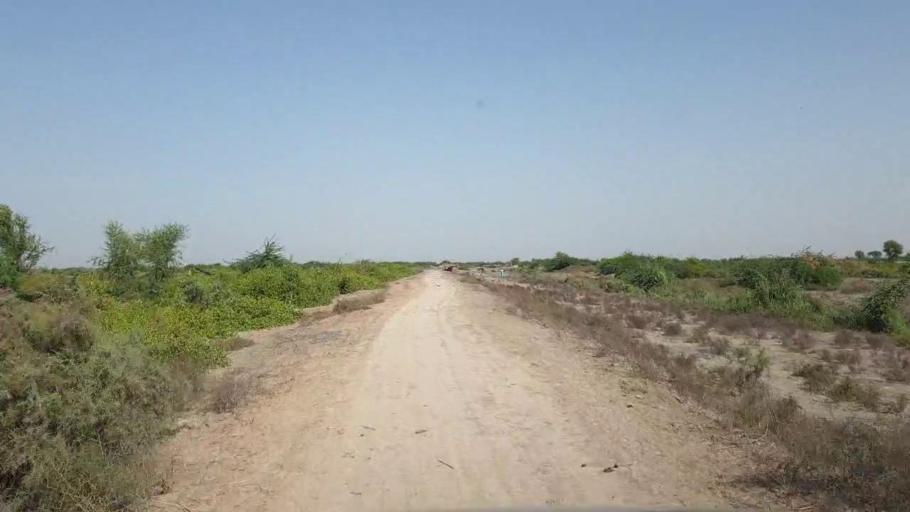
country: PK
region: Sindh
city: Tando Bago
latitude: 24.7061
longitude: 69.0712
